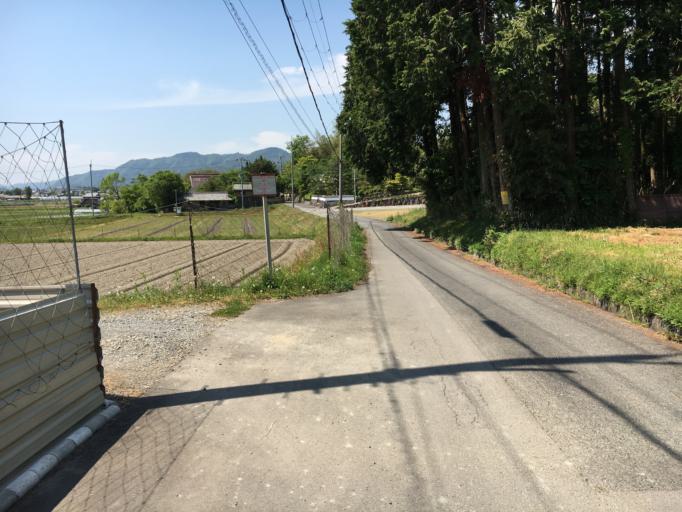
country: JP
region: Kyoto
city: Kameoka
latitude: 35.0713
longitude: 135.5695
